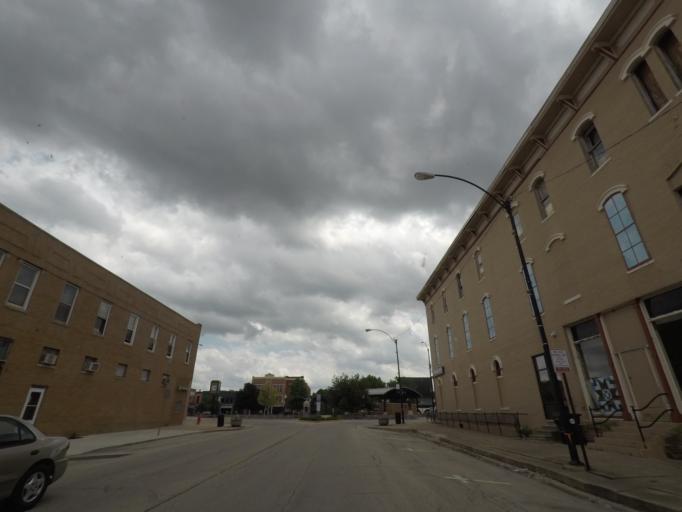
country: US
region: Illinois
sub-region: De Witt County
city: Clinton
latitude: 40.1535
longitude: -88.9606
